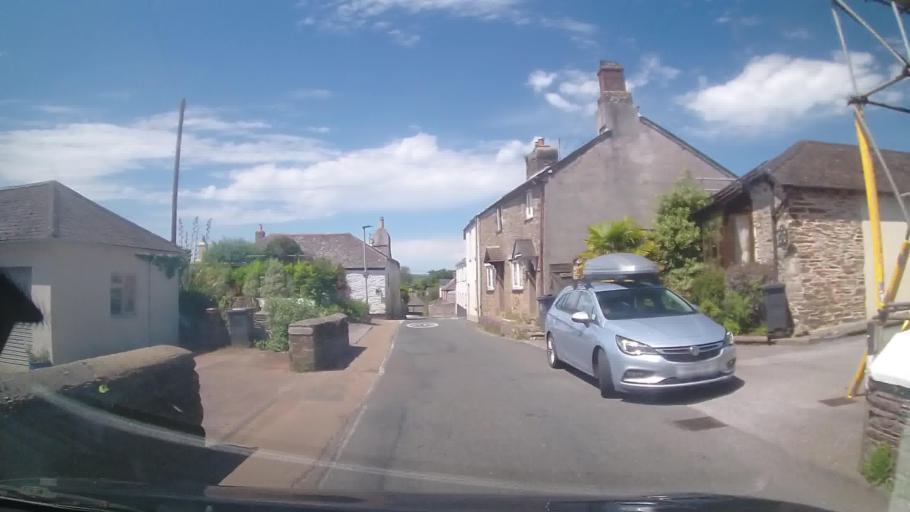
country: GB
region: England
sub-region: Devon
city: Kingsbridge
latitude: 50.2705
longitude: -3.7502
